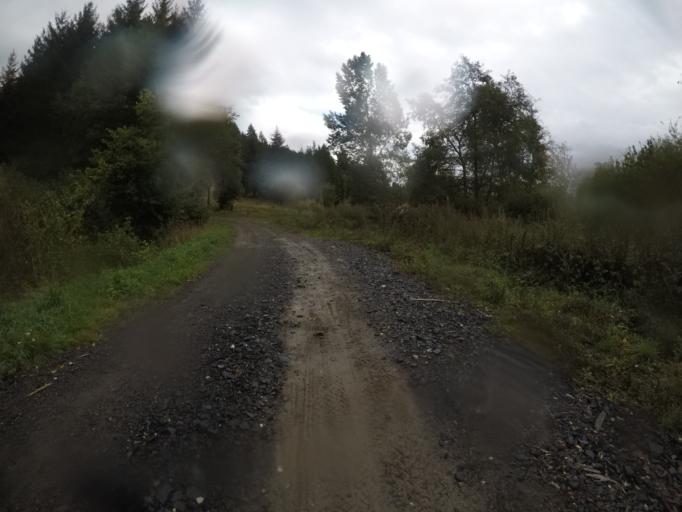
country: BE
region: Wallonia
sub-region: Province du Luxembourg
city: Fauvillers
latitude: 49.8724
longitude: 5.6863
